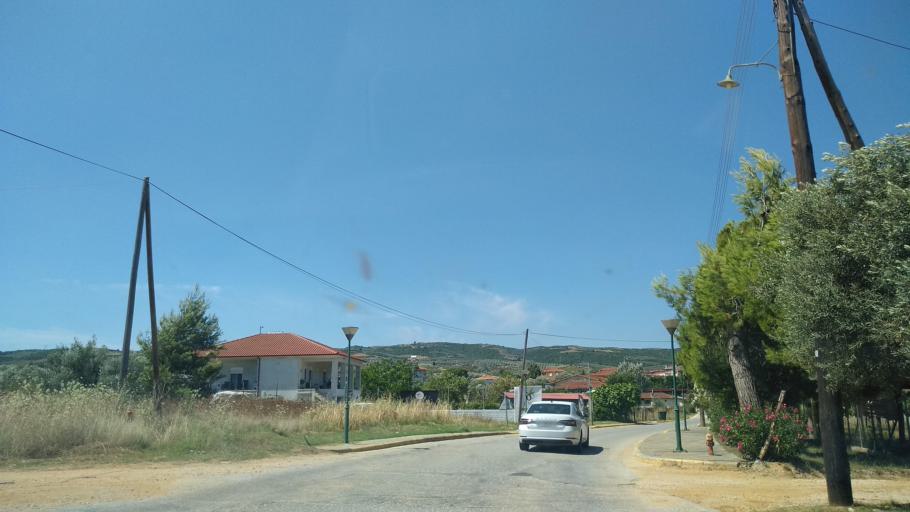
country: GR
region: Central Macedonia
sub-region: Nomos Chalkidikis
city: Agios Nikolaos
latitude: 40.3249
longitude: 23.6616
